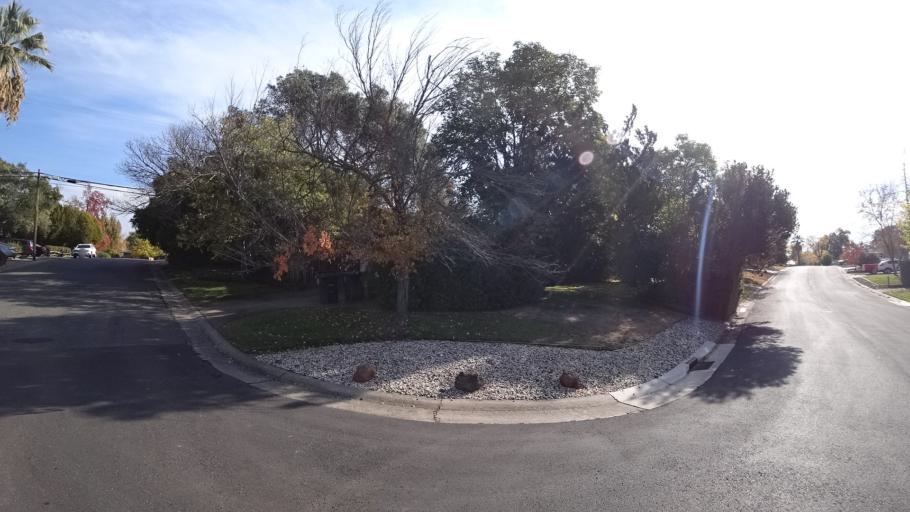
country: US
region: California
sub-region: Sacramento County
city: Fair Oaks
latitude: 38.6667
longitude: -121.2812
